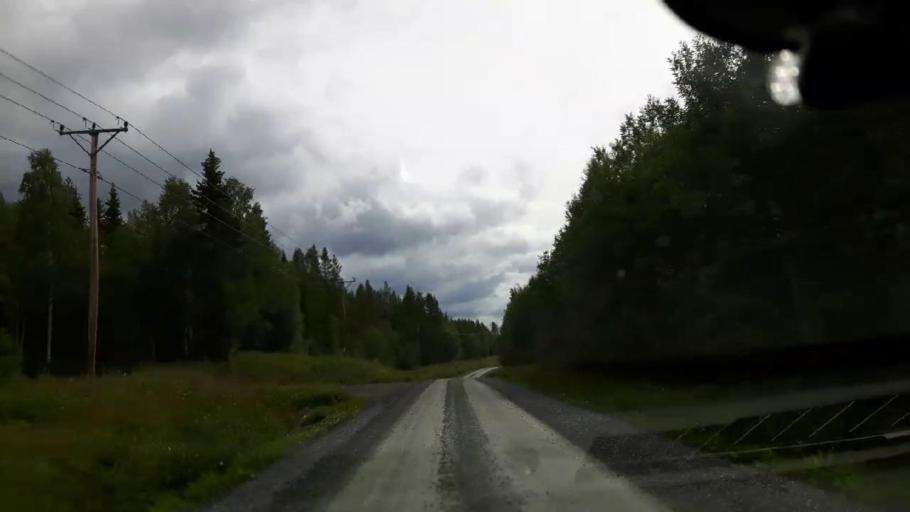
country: SE
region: Jaemtland
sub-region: Krokoms Kommun
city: Valla
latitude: 63.5949
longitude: 14.1399
